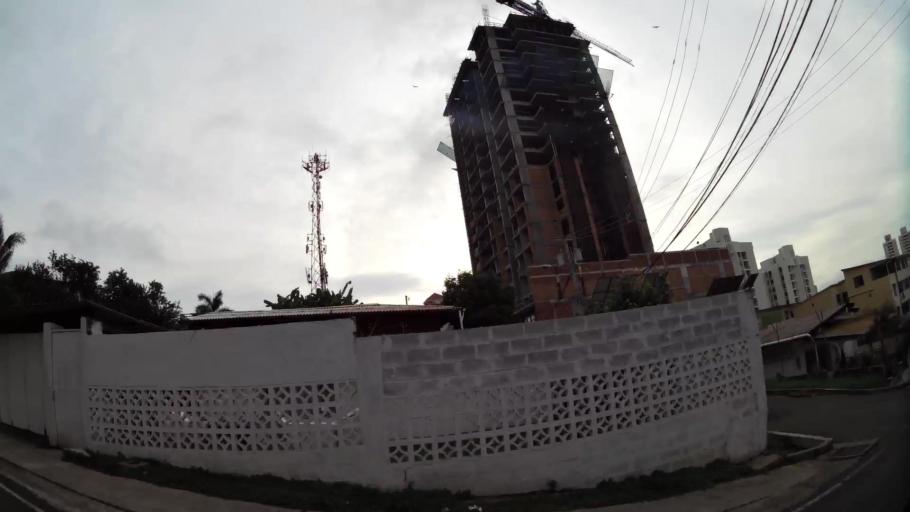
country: PA
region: Panama
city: Panama
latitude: 8.9998
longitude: -79.5135
